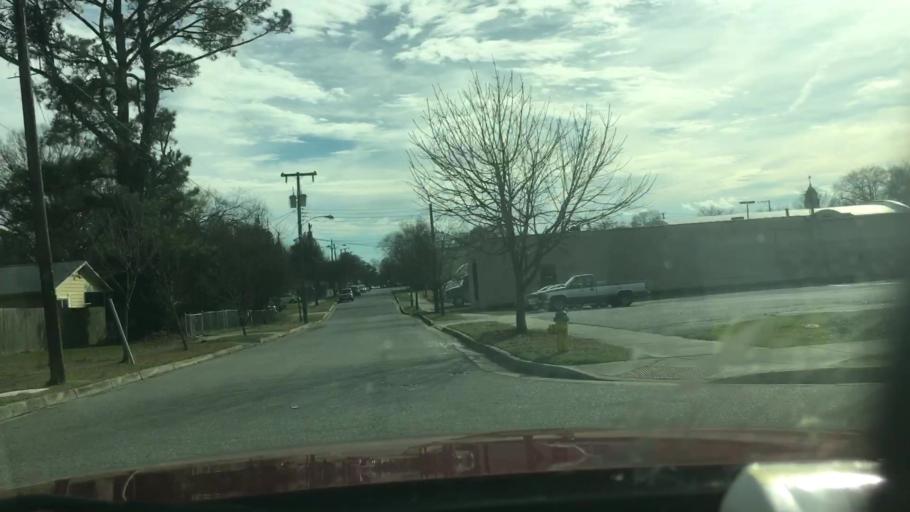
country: US
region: Virginia
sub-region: City of Norfolk
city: Norfolk
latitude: 36.8795
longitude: -76.2619
